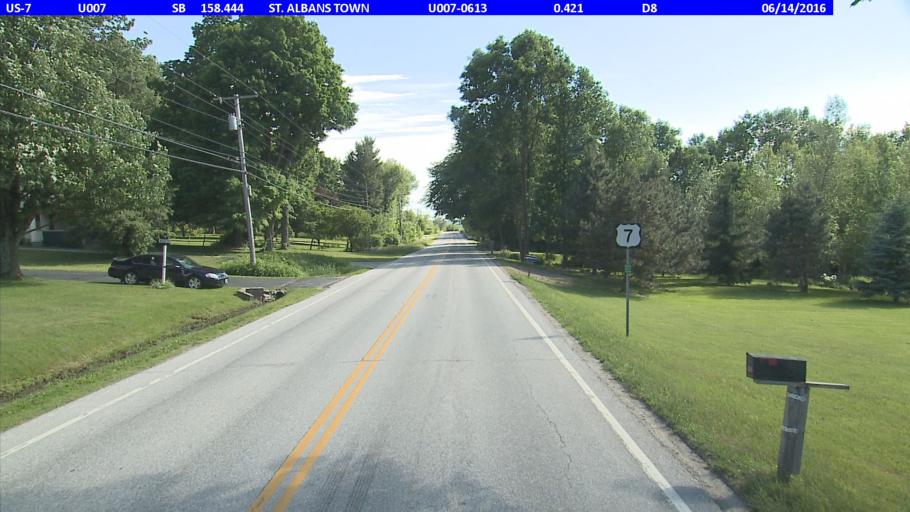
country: US
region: Vermont
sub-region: Franklin County
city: Saint Albans
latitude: 44.7858
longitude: -73.1015
